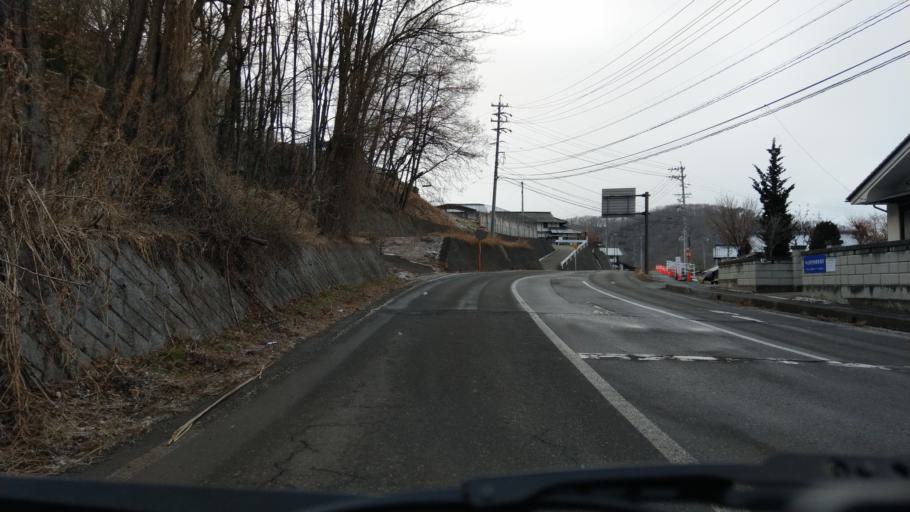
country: JP
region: Nagano
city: Kamimaruko
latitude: 36.3259
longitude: 138.3457
